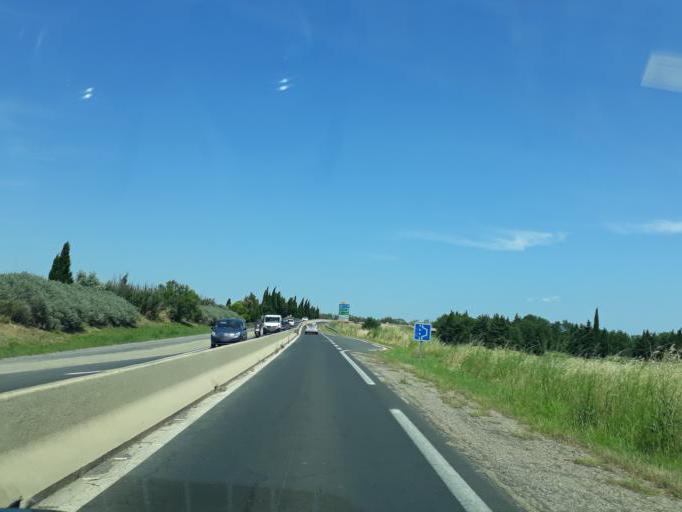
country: FR
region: Languedoc-Roussillon
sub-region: Departement de l'Herault
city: Vias
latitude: 43.3076
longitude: 3.4265
